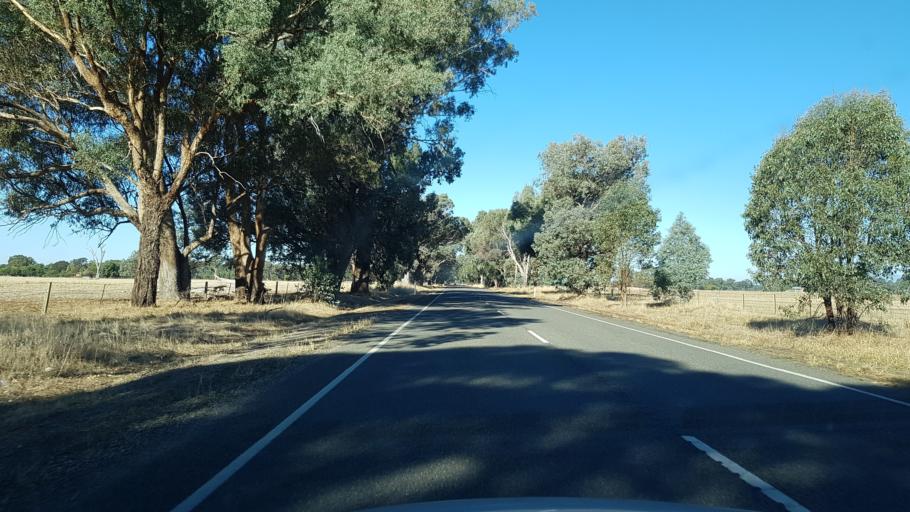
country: AU
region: Victoria
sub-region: Wangaratta
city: Wangaratta
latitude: -36.4365
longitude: 146.3306
